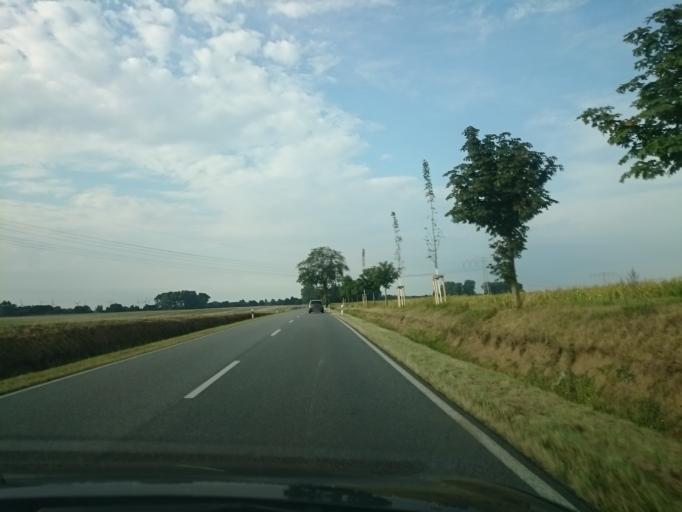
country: DE
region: Mecklenburg-Vorpommern
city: Demmin
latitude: 53.8840
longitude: 13.0276
